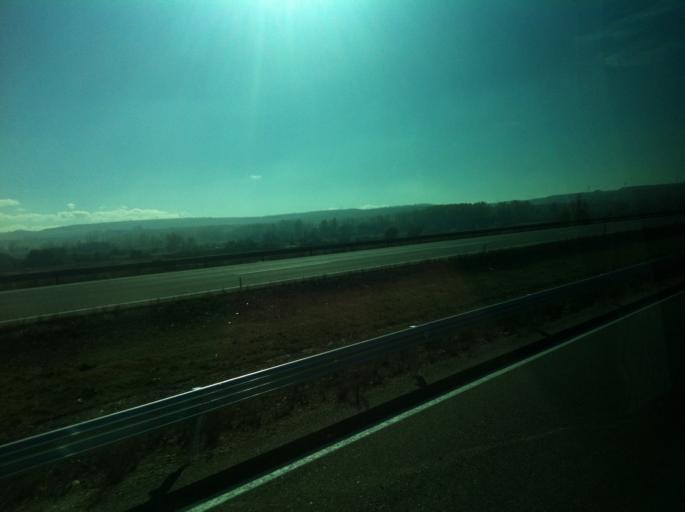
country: ES
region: Castille and Leon
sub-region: Provincia de Burgos
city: Cardenajimeno
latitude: 42.3424
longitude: -3.6071
